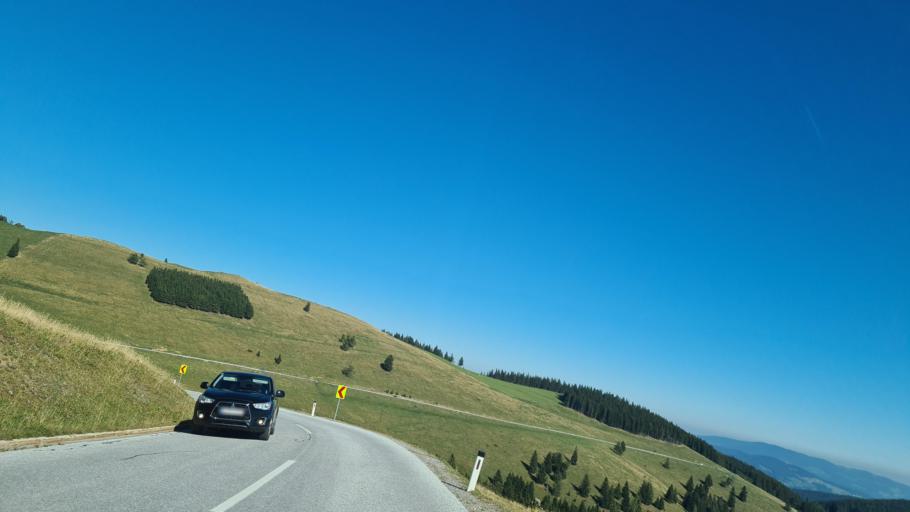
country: AT
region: Styria
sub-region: Politischer Bezirk Weiz
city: Gasen
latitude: 47.3535
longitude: 15.5683
